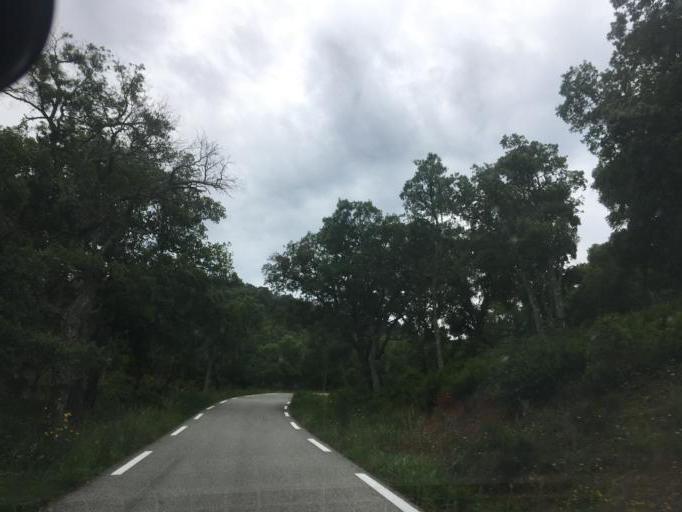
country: FR
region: Provence-Alpes-Cote d'Azur
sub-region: Departement du Var
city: Pierrefeu-du-Var
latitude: 43.2213
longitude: 6.2203
